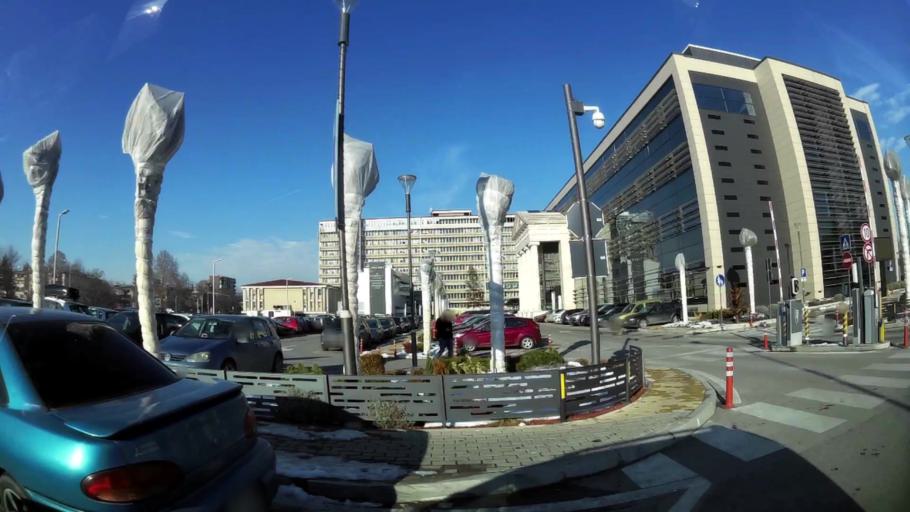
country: MK
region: Karpos
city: Skopje
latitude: 42.0037
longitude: 21.4029
